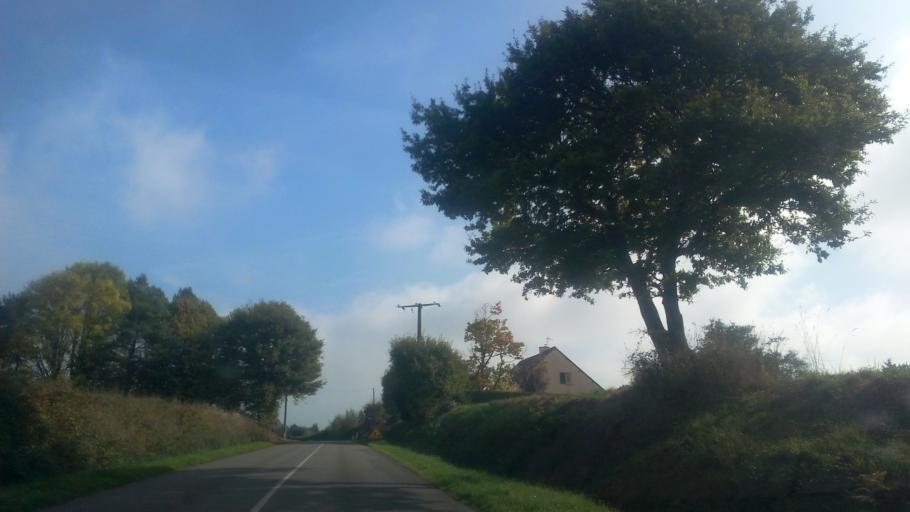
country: FR
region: Pays de la Loire
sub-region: Departement de la Loire-Atlantique
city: Conquereuil
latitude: 47.6259
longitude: -1.7602
